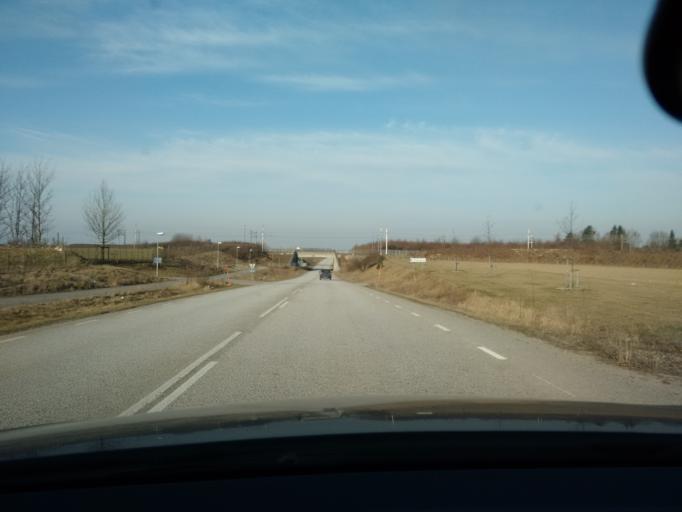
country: SE
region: Skane
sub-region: Lunds Kommun
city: Lund
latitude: 55.7441
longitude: 13.1980
